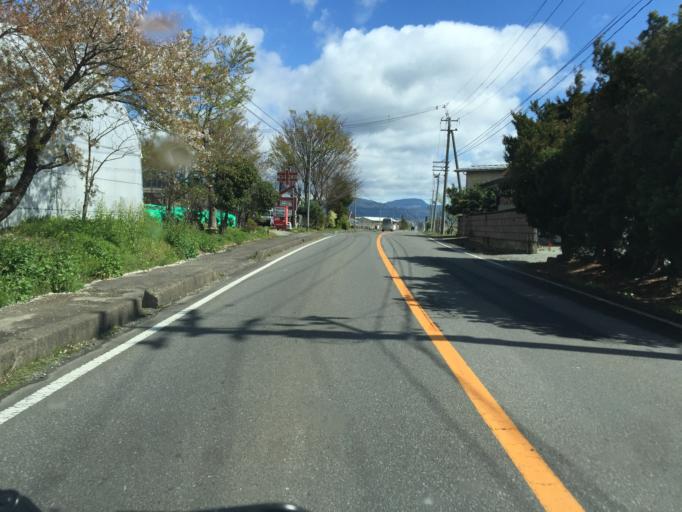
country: JP
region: Fukushima
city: Fukushima-shi
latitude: 37.7784
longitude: 140.3889
